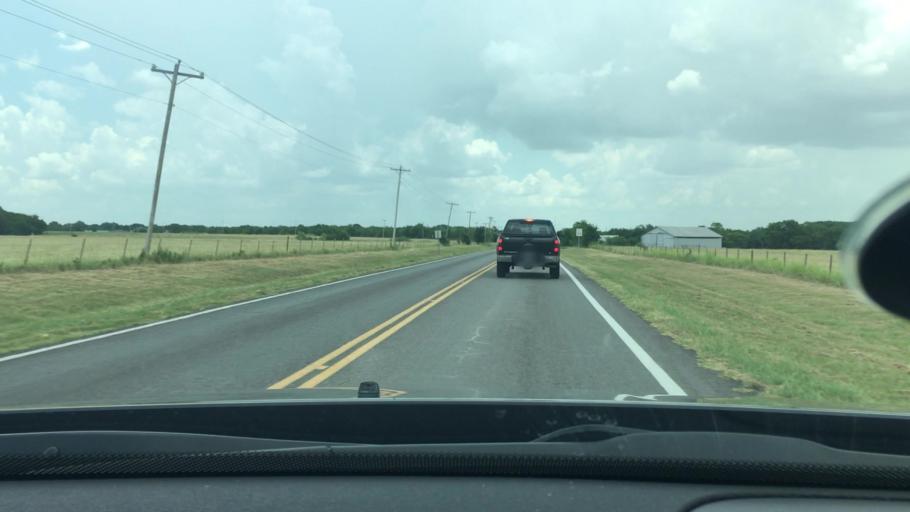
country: US
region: Oklahoma
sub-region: Marshall County
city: Madill
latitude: 34.0743
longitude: -96.7882
